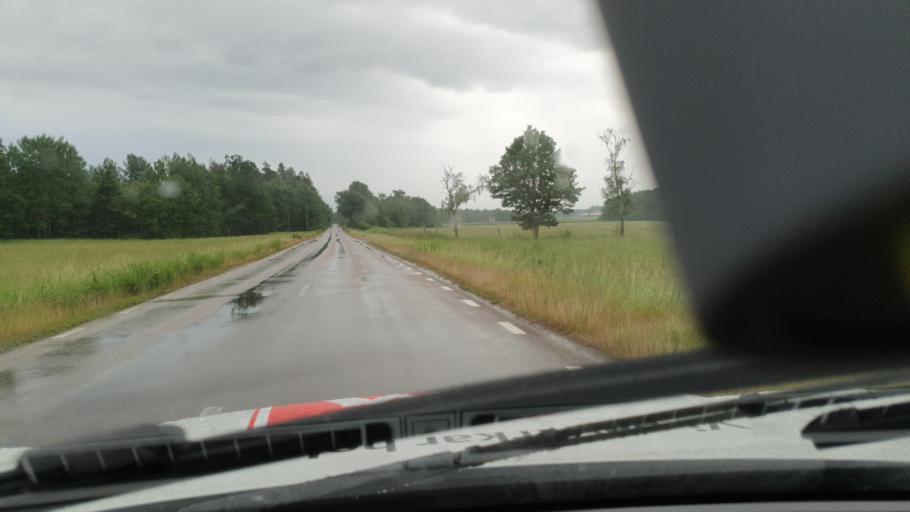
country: SE
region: Vaestra Goetaland
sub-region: Mariestads Kommun
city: Mariestad
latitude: 58.7709
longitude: 13.9061
